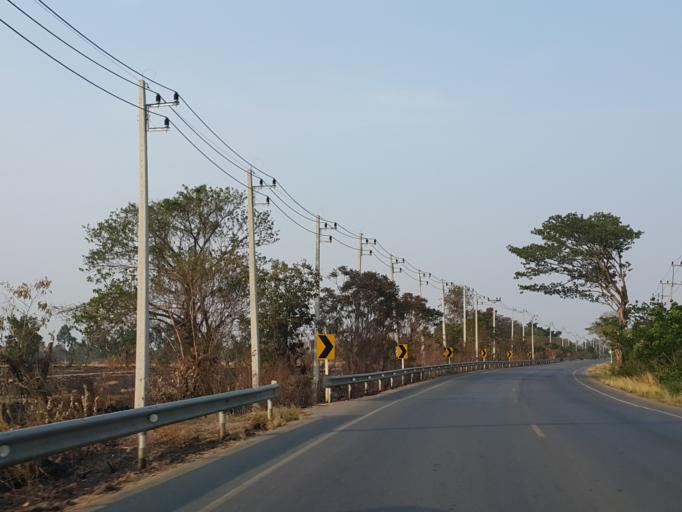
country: TH
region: Chai Nat
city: Sankhaburi
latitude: 15.0765
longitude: 100.1801
